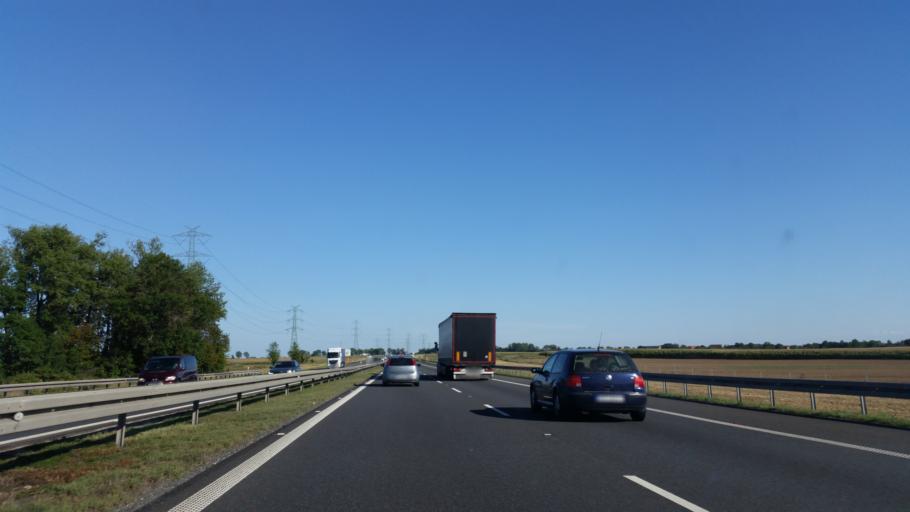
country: PL
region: Lower Silesian Voivodeship
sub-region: Powiat olawski
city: Wierzbno
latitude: 50.9011
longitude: 17.1699
